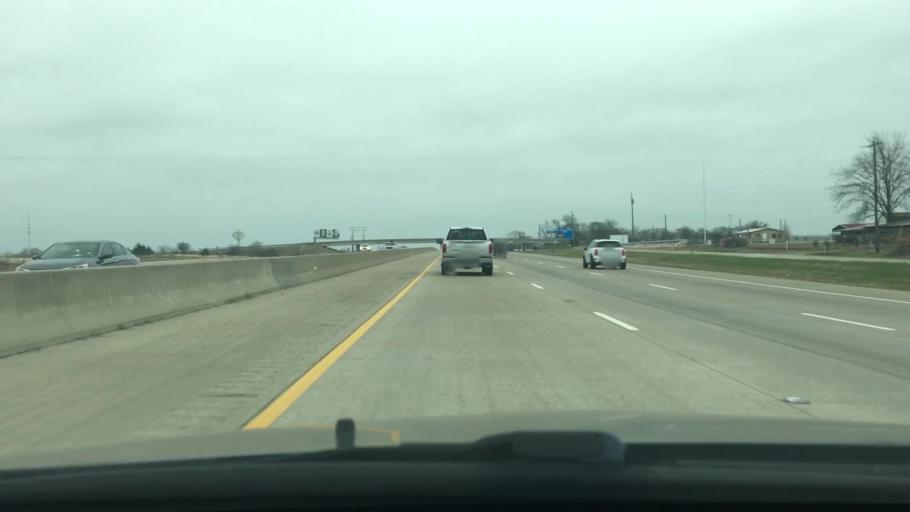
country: US
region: Texas
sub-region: Ellis County
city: Ennis
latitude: 32.2605
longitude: -96.5054
